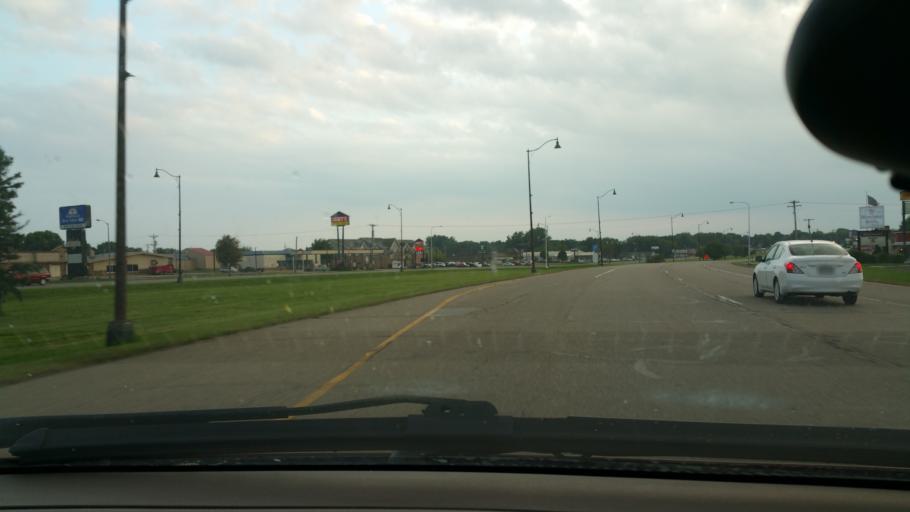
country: US
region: Minnesota
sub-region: Freeborn County
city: Albert Lea
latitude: 43.6567
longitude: -93.3356
